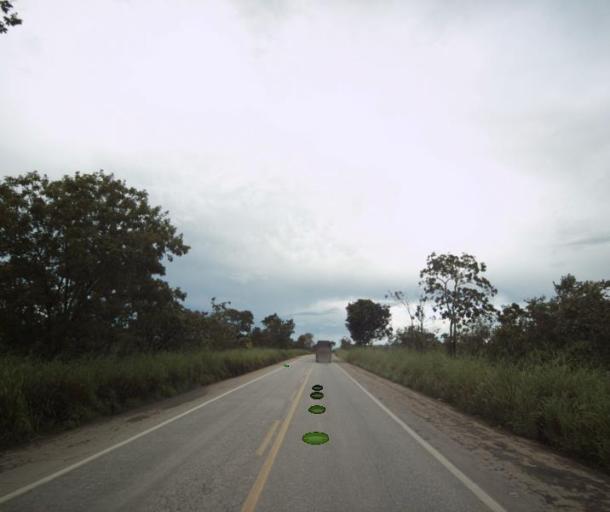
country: BR
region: Goias
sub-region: Porangatu
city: Porangatu
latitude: -13.5719
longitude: -49.0463
